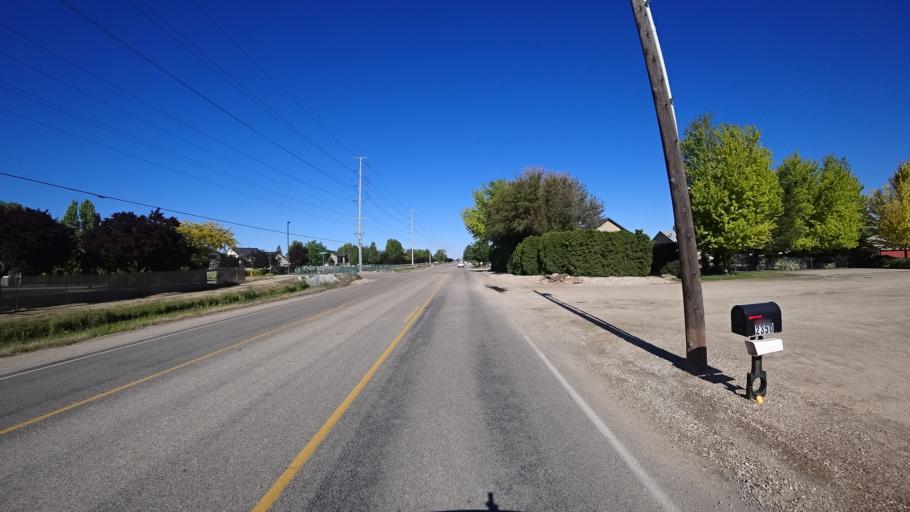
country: US
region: Idaho
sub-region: Ada County
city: Meridian
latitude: 43.6479
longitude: -116.4210
